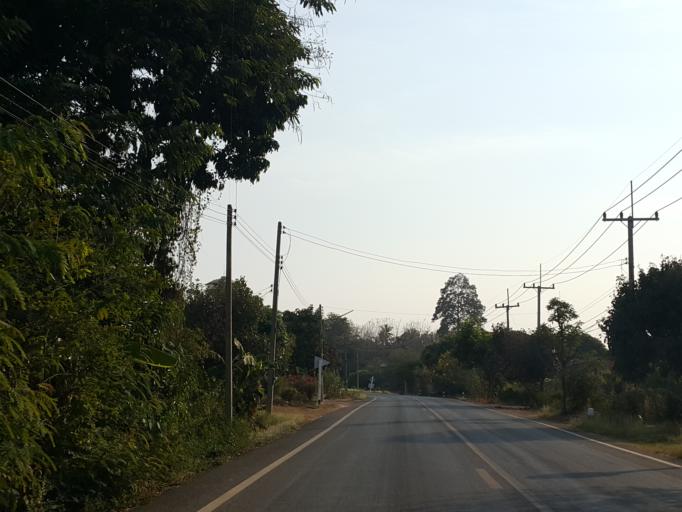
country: TH
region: Uttaradit
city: Phichai
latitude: 17.1696
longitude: 100.1077
